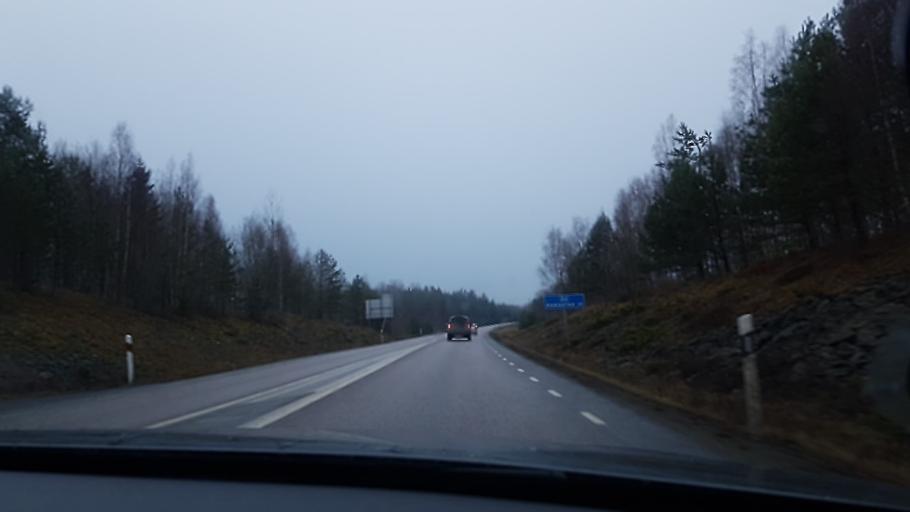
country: SE
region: Vaestra Goetaland
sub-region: Toreboda Kommun
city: Toereboda
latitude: 58.8285
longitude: 13.9888
